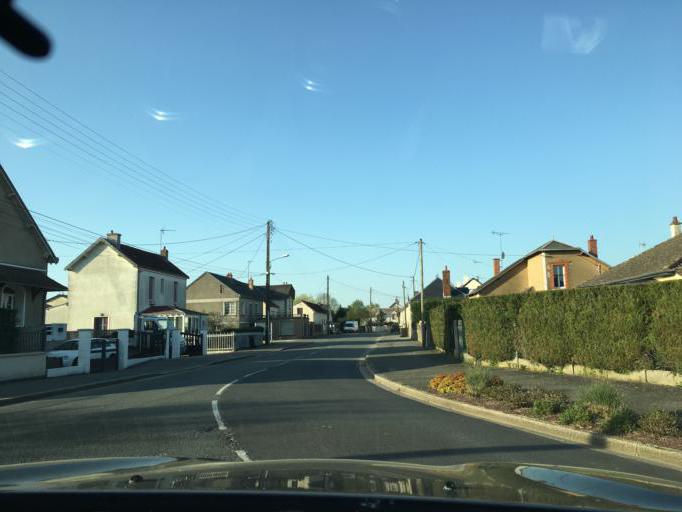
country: FR
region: Centre
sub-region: Departement du Loir-et-Cher
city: Ouzouer-le-Marche
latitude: 47.9069
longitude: 1.5256
